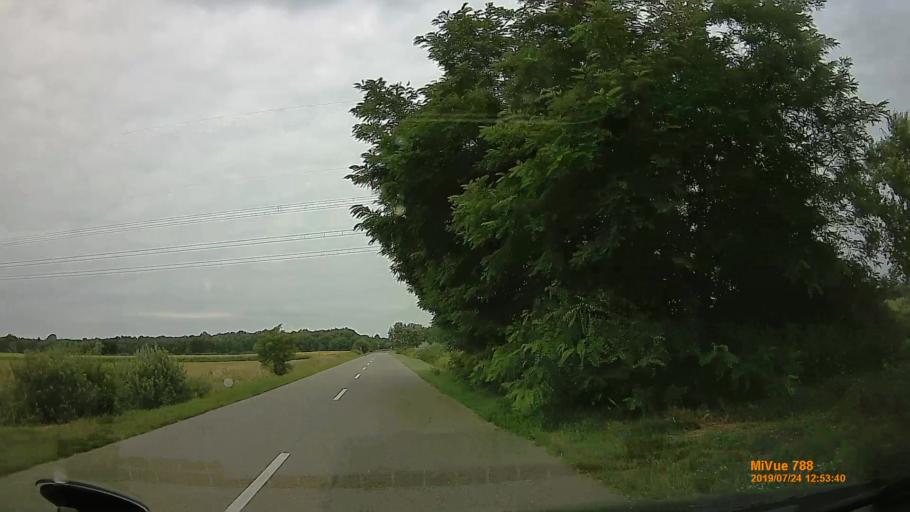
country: HU
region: Szabolcs-Szatmar-Bereg
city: Aranyosapati
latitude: 48.2071
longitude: 22.3033
